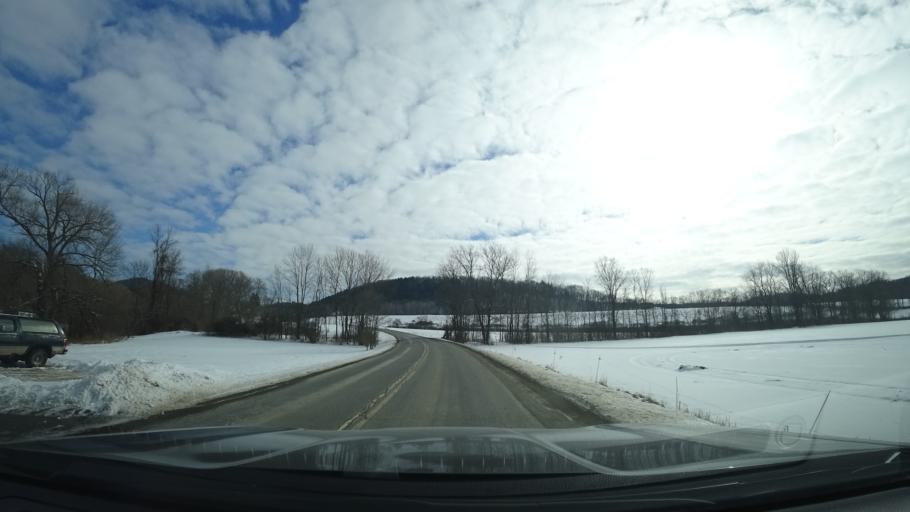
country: US
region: New York
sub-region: Washington County
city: Fort Edward
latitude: 43.2439
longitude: -73.4750
